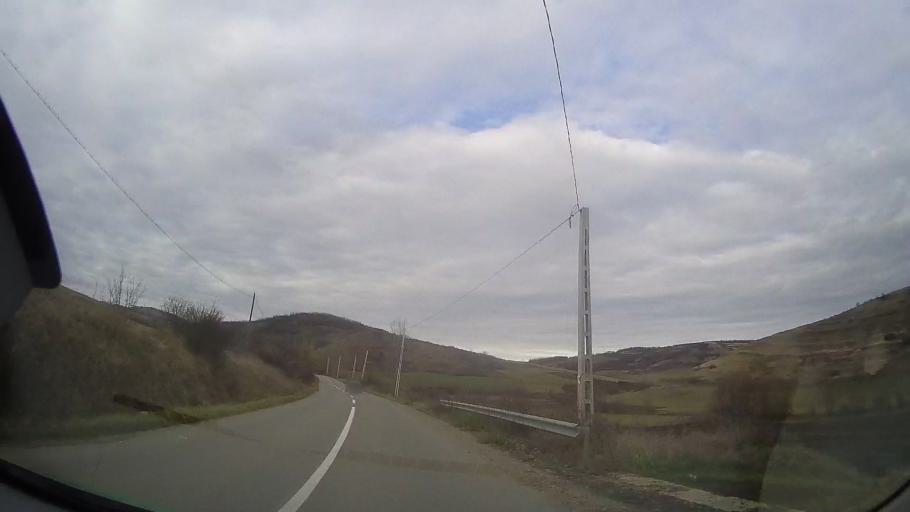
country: RO
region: Bistrita-Nasaud
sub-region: Comuna Milas
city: Milas
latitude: 46.8368
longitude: 24.4480
